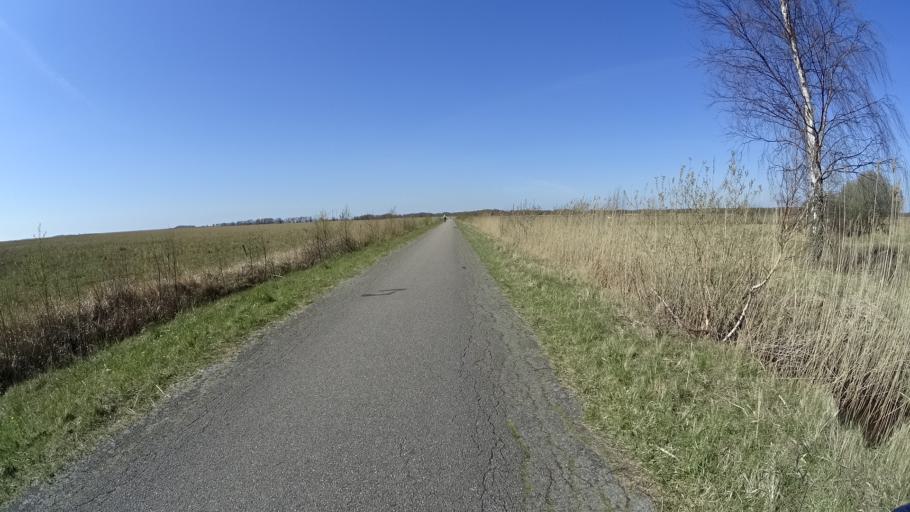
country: DK
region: Capital Region
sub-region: Tarnby Kommune
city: Tarnby
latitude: 55.6155
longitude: 12.5597
